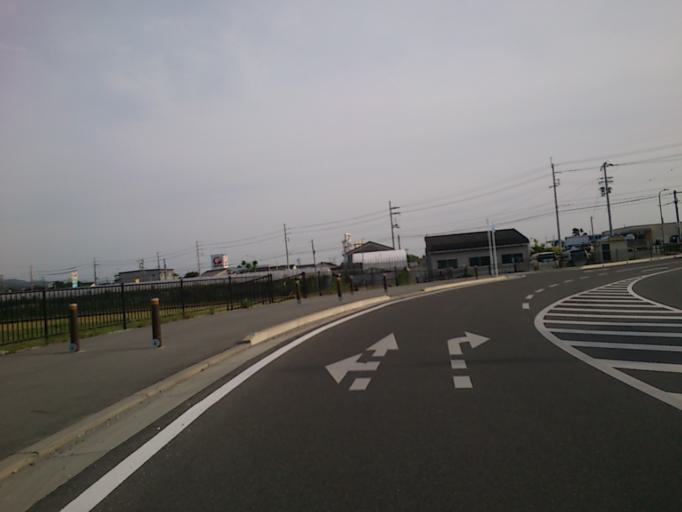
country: JP
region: Nara
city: Nara-shi
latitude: 34.7531
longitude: 135.8150
